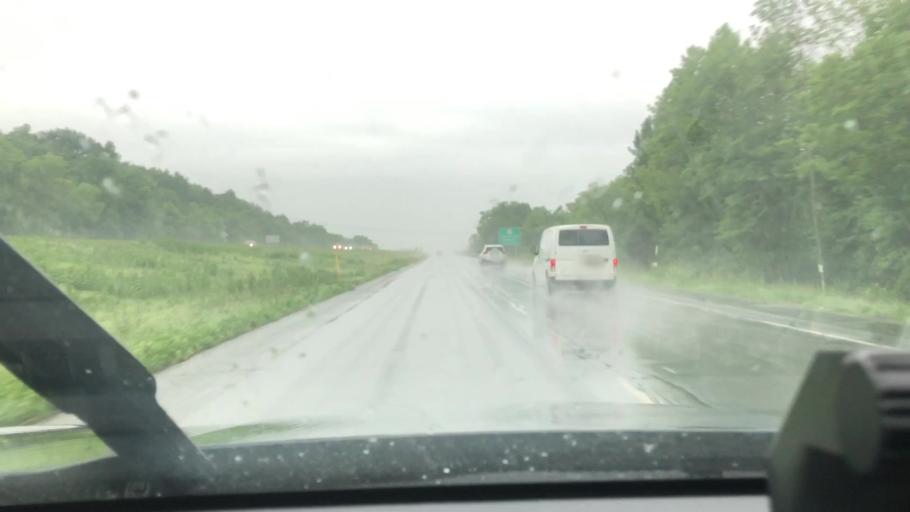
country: US
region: Pennsylvania
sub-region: Northampton County
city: Belfast
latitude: 40.7662
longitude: -75.2758
